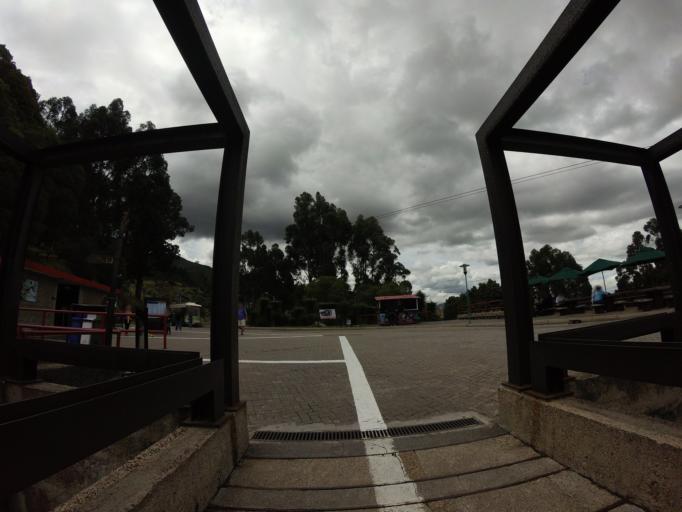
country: CO
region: Cundinamarca
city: Zipaquira
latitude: 5.0193
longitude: -74.0092
